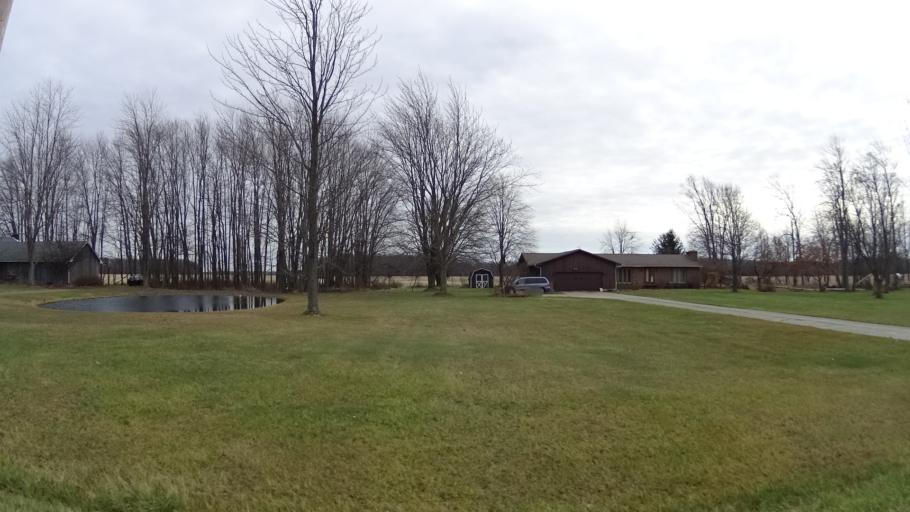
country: US
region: Ohio
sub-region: Lorain County
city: Camden
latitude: 41.2004
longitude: -82.2680
